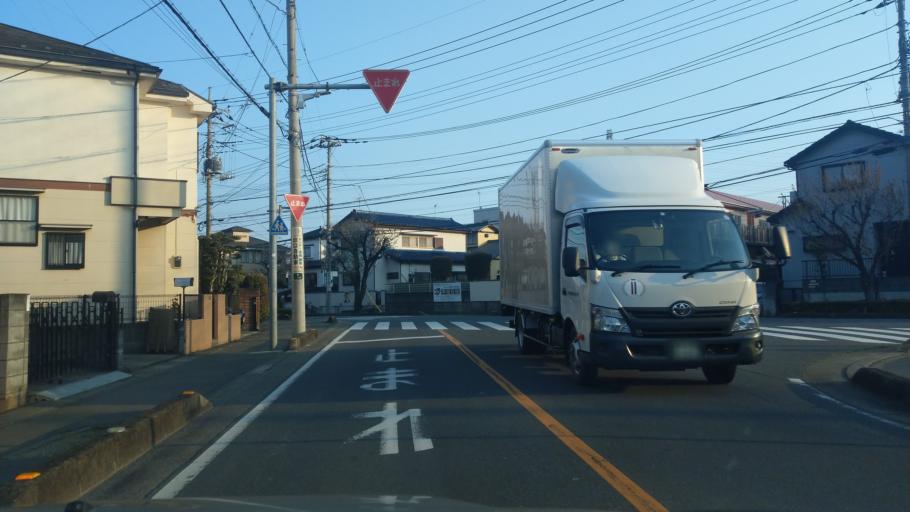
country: JP
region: Saitama
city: Ageoshimo
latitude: 36.0087
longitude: 139.6016
